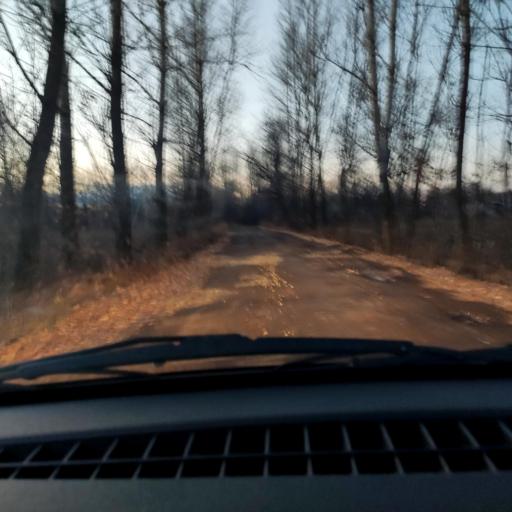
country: RU
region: Bashkortostan
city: Ufa
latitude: 54.6540
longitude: 55.8895
